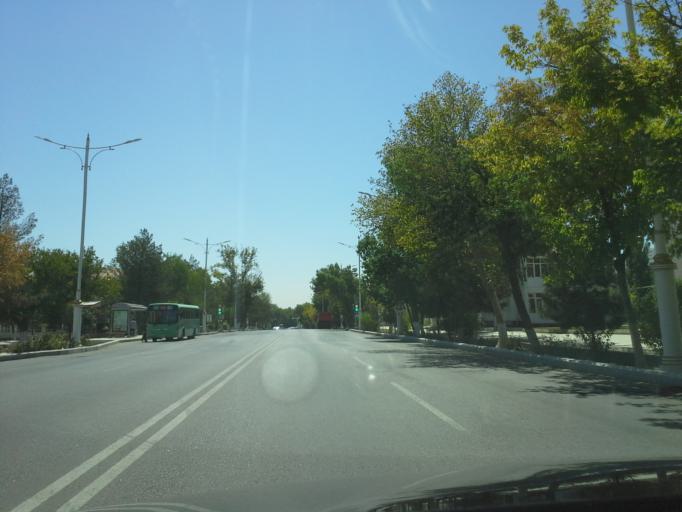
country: TM
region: Ahal
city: Ashgabat
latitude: 37.9481
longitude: 58.3494
